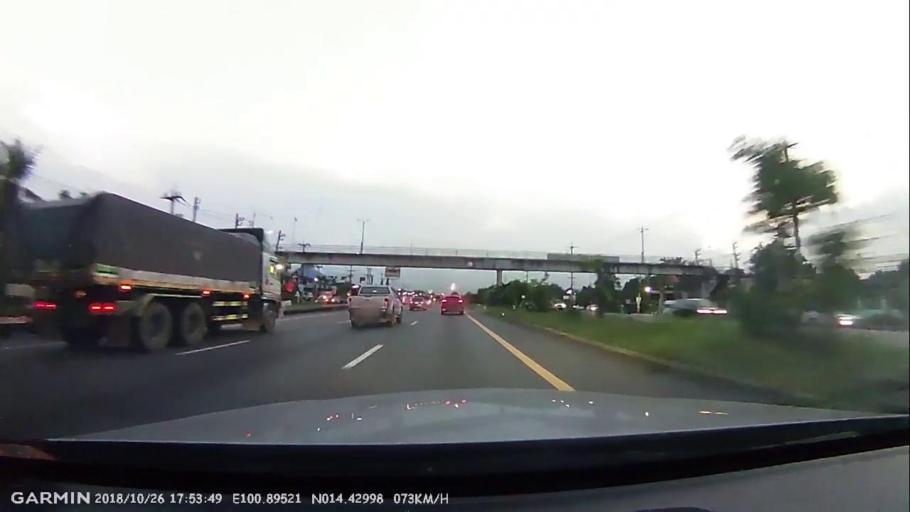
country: TH
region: Sara Buri
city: Nong Khae
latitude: 14.4297
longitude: 100.8952
